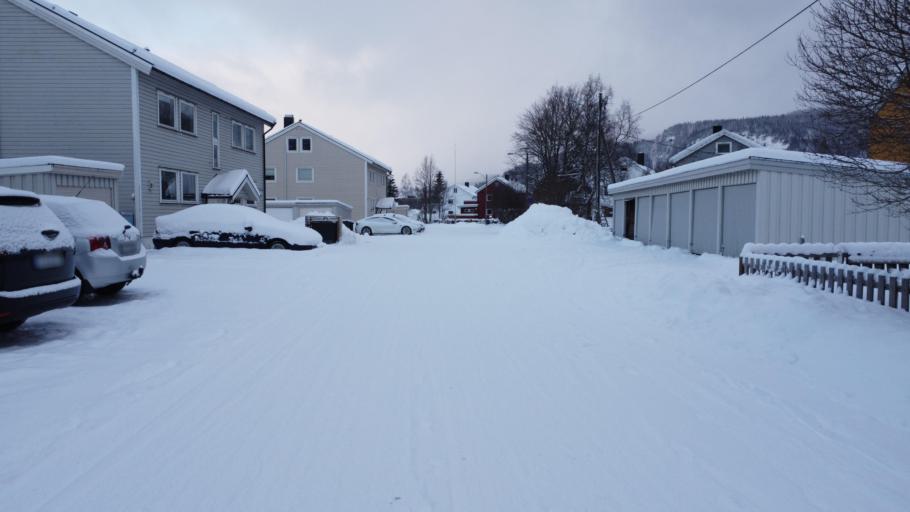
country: NO
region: Nordland
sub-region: Rana
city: Mo i Rana
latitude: 66.3193
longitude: 14.1631
